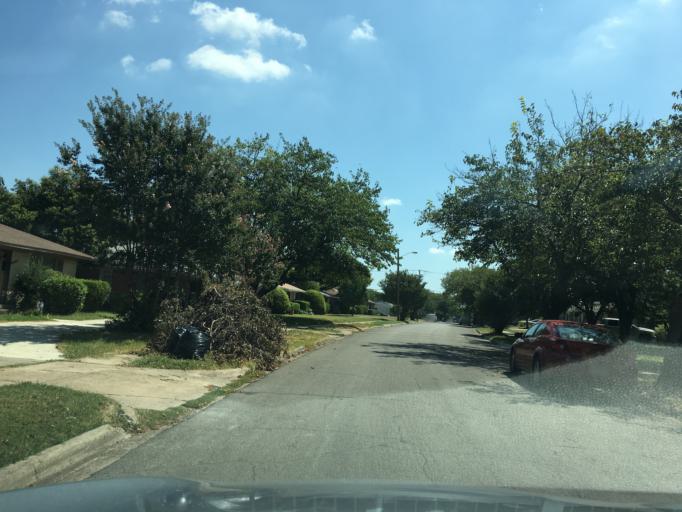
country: US
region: Texas
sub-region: Dallas County
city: Garland
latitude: 32.8524
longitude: -96.6848
